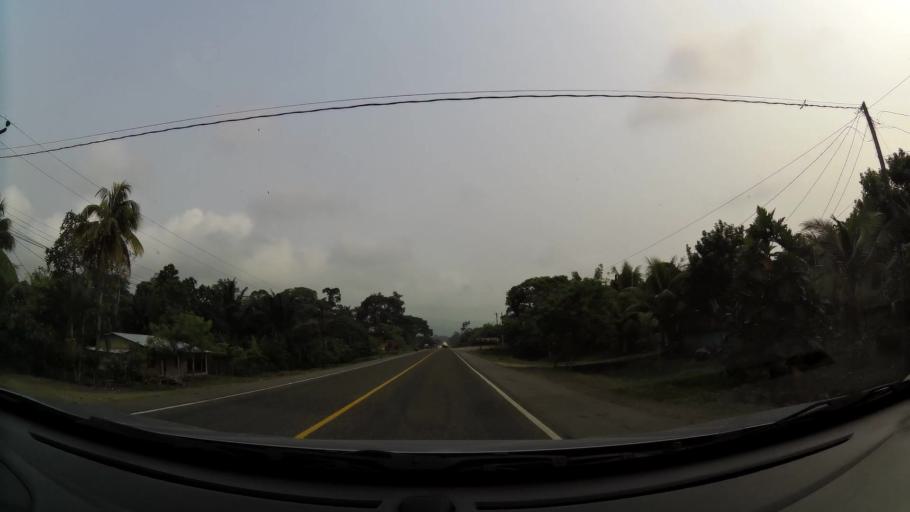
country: HN
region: Atlantida
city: Mezapa
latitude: 15.6121
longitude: -87.6138
